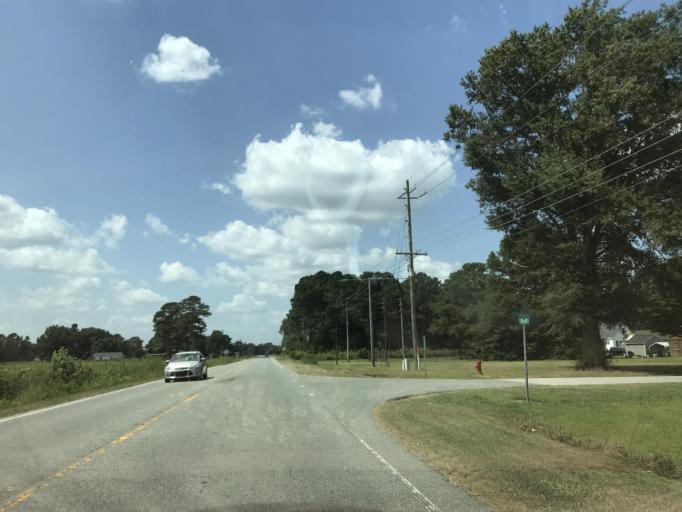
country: US
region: North Carolina
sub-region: Sampson County
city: Plain View
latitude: 35.2475
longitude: -78.3628
